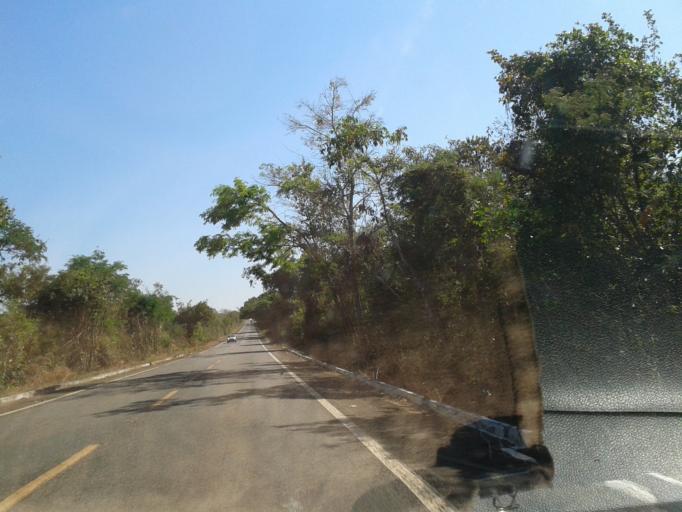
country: BR
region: Goias
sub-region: Sao Miguel Do Araguaia
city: Sao Miguel do Araguaia
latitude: -13.9336
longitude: -50.3202
